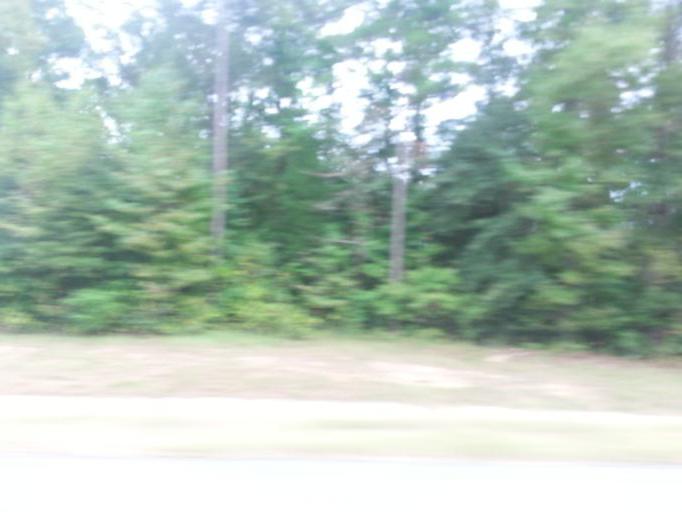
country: US
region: Alabama
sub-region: Conecuh County
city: Evergreen
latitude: 31.4730
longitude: -86.9522
